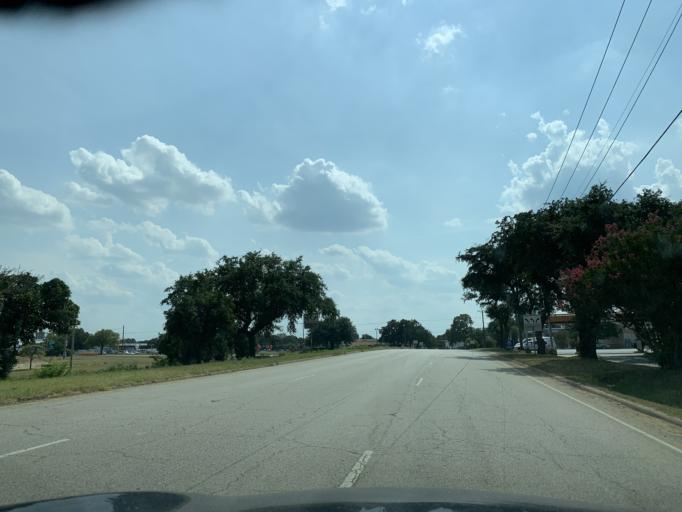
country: US
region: Texas
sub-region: Tarrant County
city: Richland Hills
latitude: 32.8109
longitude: -97.2104
